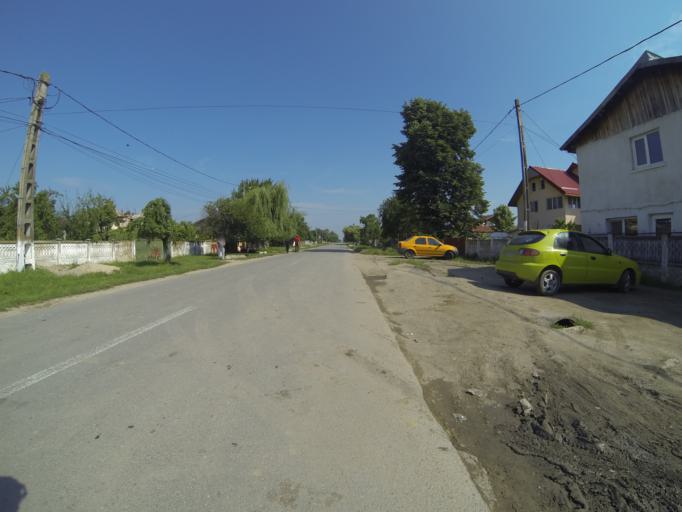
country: RO
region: Gorj
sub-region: Comuna Crusetu
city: Crusetu
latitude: 44.6034
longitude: 23.6905
